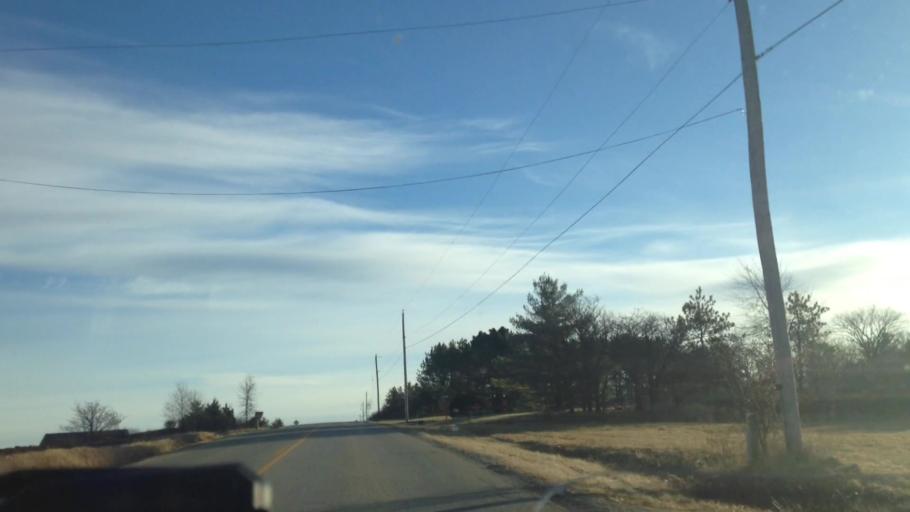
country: US
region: Wisconsin
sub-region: Washington County
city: Jackson
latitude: 43.2949
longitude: -88.1556
